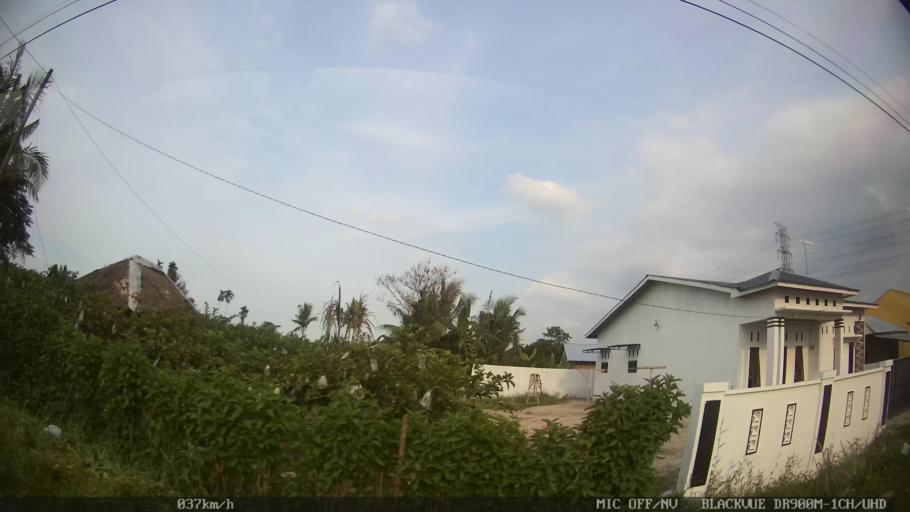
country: ID
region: North Sumatra
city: Sunggal
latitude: 3.5852
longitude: 98.5515
